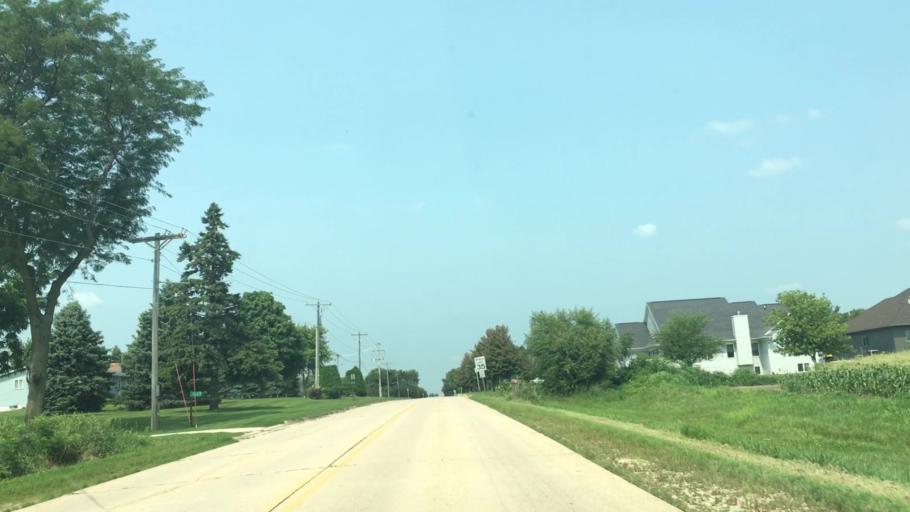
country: US
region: Iowa
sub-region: Fayette County
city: Oelwein
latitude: 42.6740
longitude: -91.8937
